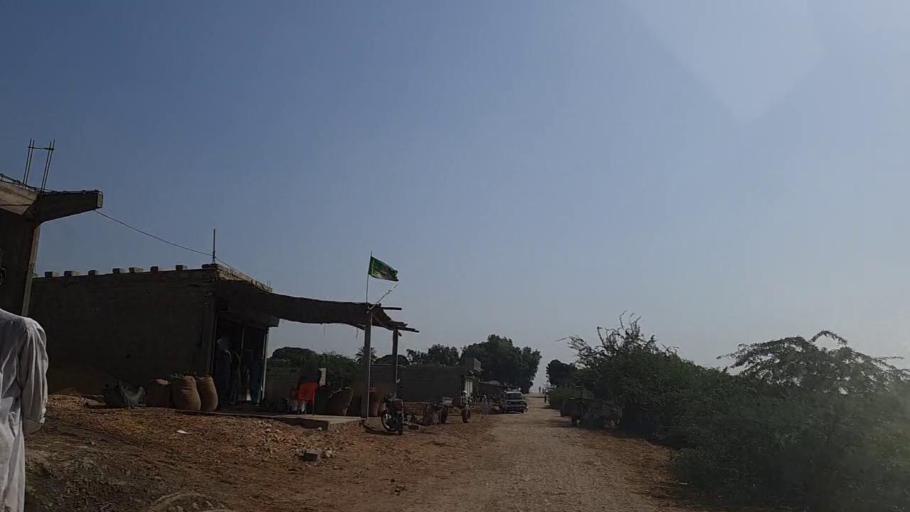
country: PK
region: Sindh
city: Daro Mehar
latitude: 24.7222
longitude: 68.0730
